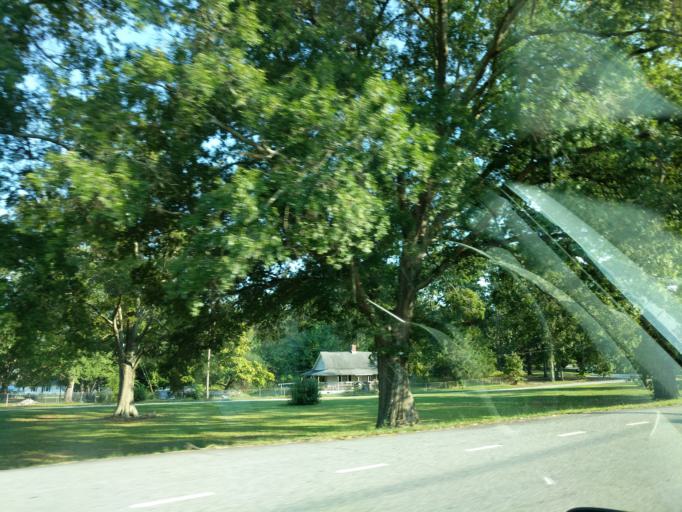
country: US
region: South Carolina
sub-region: Anderson County
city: Williamston
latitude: 34.6461
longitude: -82.4636
